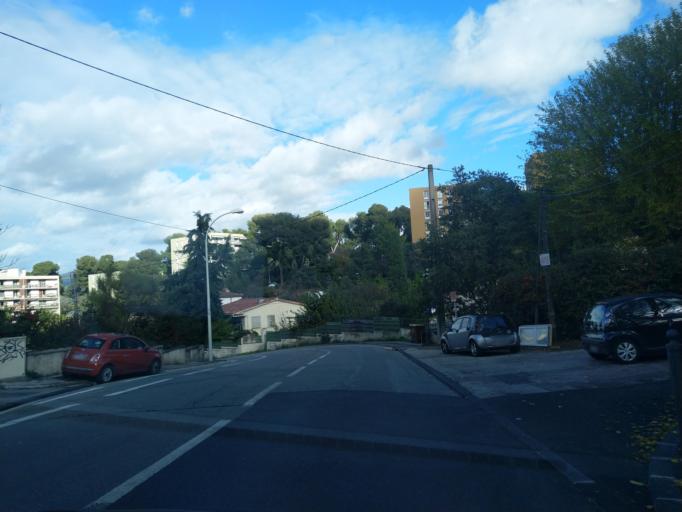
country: FR
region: Provence-Alpes-Cote d'Azur
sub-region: Departement des Bouches-du-Rhone
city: Marseille 12
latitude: 43.3231
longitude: 5.4403
